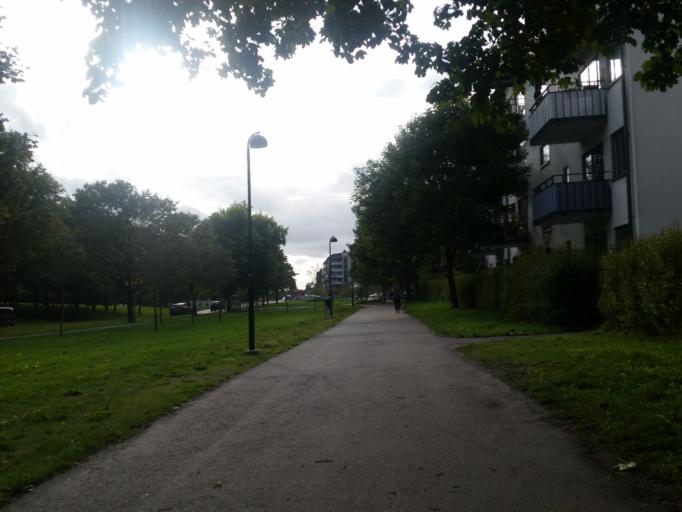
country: SE
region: Stockholm
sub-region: Stockholms Kommun
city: Arsta
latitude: 59.2902
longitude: 18.0999
